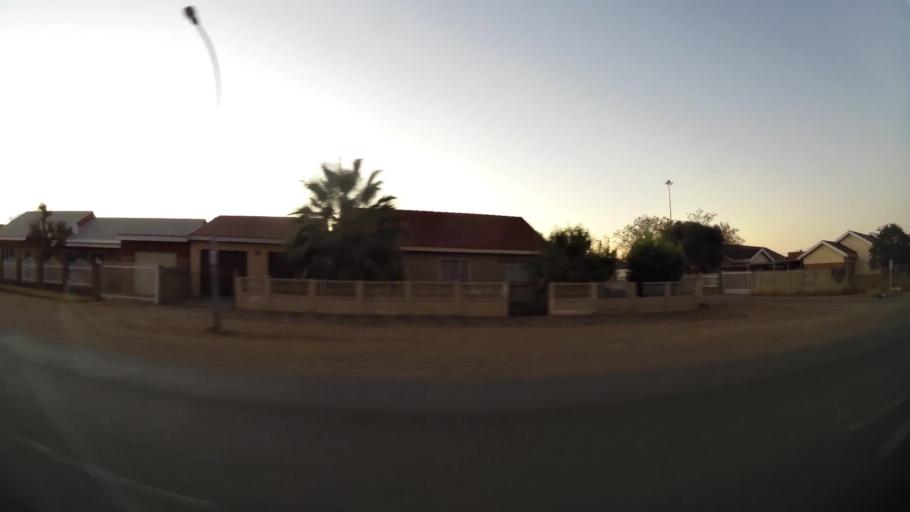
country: ZA
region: Northern Cape
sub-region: Frances Baard District Municipality
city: Kimberley
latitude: -28.7230
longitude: 24.7658
